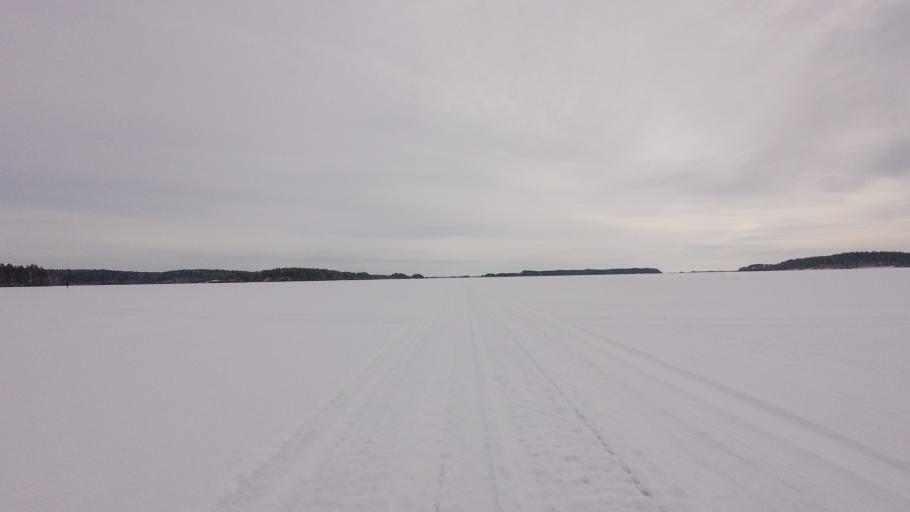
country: FI
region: Southern Savonia
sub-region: Savonlinna
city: Rantasalmi
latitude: 62.0990
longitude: 28.4737
